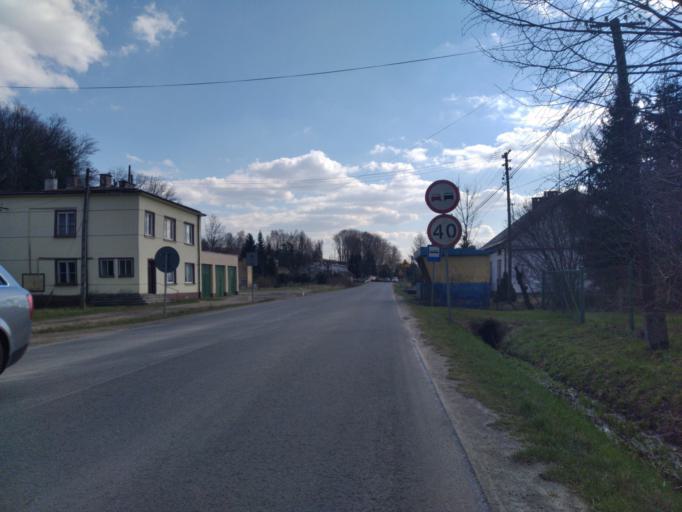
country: PL
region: Subcarpathian Voivodeship
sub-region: Powiat brzozowski
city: Grabownica Starzenska
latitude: 49.6671
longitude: 22.0832
